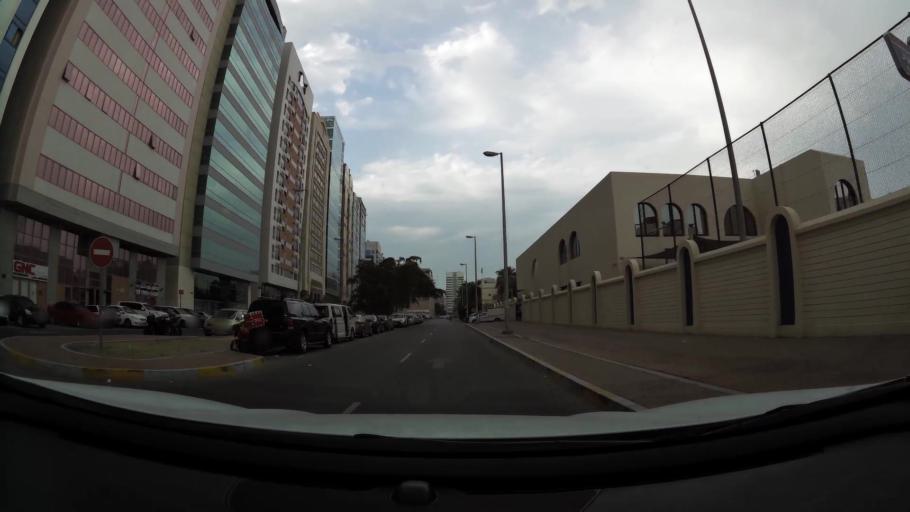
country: AE
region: Abu Dhabi
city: Abu Dhabi
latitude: 24.4749
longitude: 54.3754
